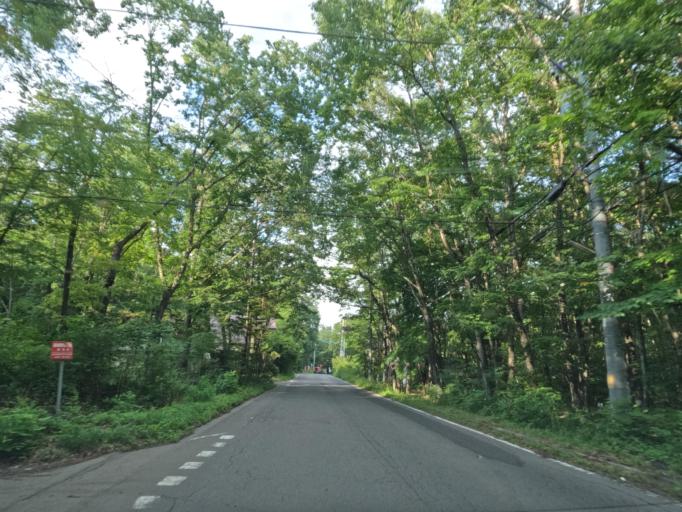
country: JP
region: Nagano
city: Komoro
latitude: 36.4689
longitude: 138.5638
